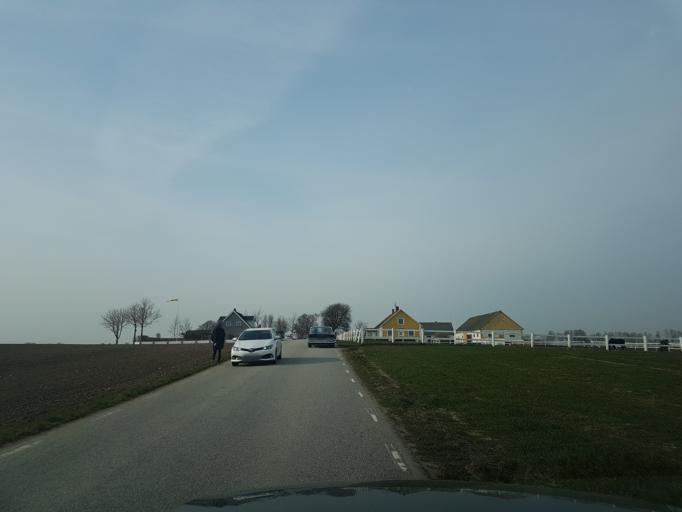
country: SE
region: Skane
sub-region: Ystads Kommun
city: Ystad
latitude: 55.4568
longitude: 13.8285
